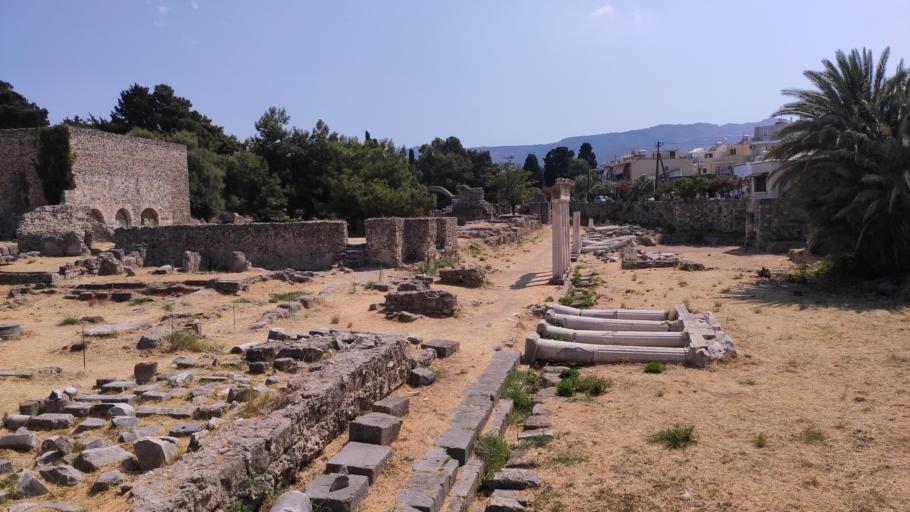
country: GR
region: South Aegean
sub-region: Nomos Dodekanisou
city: Kos
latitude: 36.8920
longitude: 27.2847
